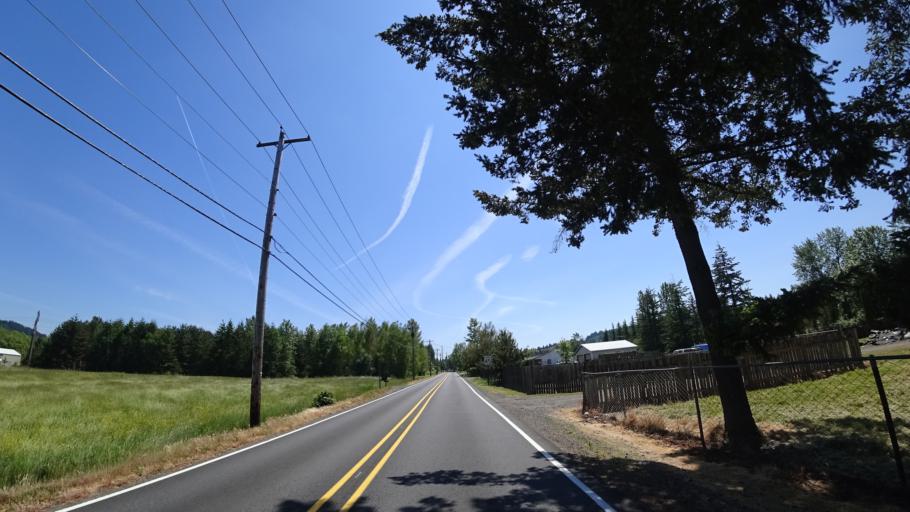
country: US
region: Oregon
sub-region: Clackamas County
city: Happy Valley
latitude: 45.4643
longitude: -122.4858
